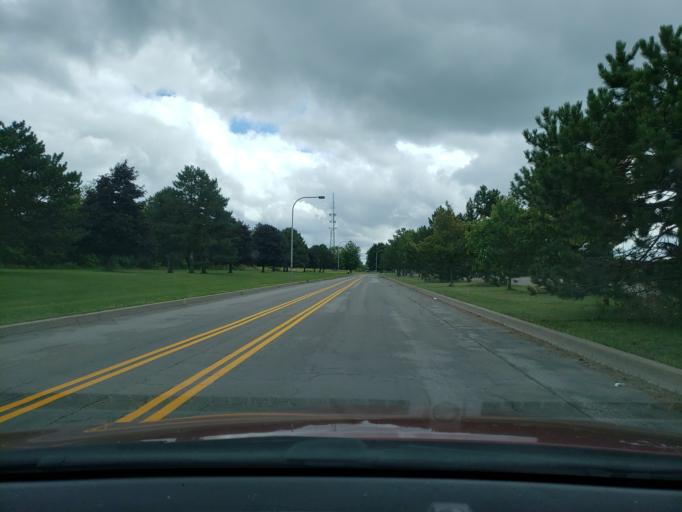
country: US
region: New York
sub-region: Monroe County
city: North Gates
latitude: 43.1566
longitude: -77.7370
